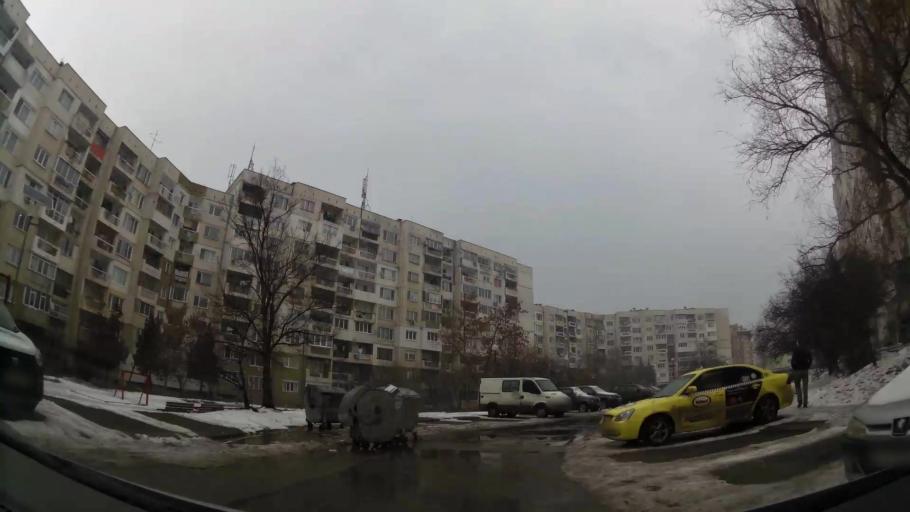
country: BG
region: Sofiya
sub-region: Obshtina Bozhurishte
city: Bozhurishte
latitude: 42.6880
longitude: 23.2450
